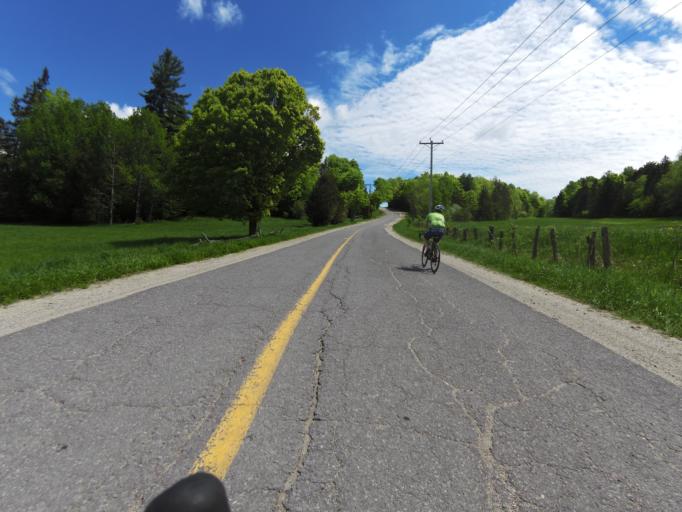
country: CA
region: Quebec
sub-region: Outaouais
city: Wakefield
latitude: 45.6909
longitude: -75.9857
